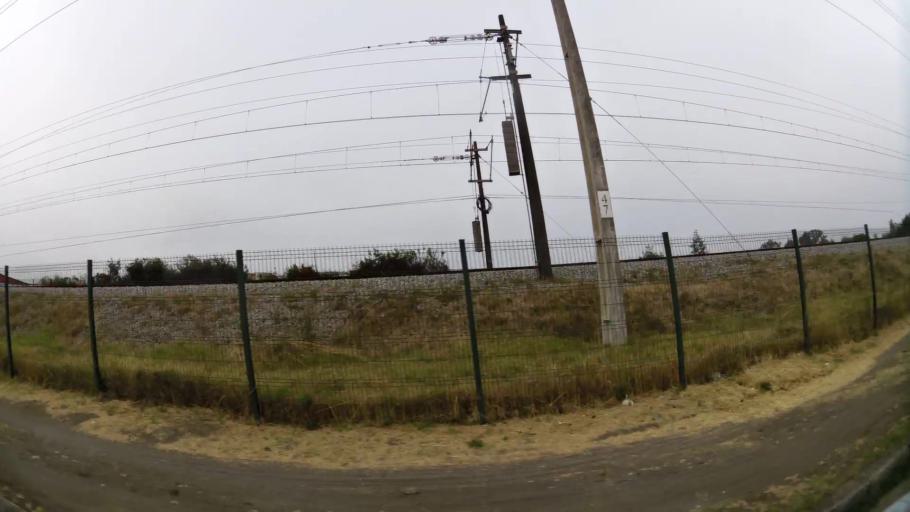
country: CL
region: Biobio
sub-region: Provincia de Concepcion
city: Concepcion
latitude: -36.7946
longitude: -73.0830
